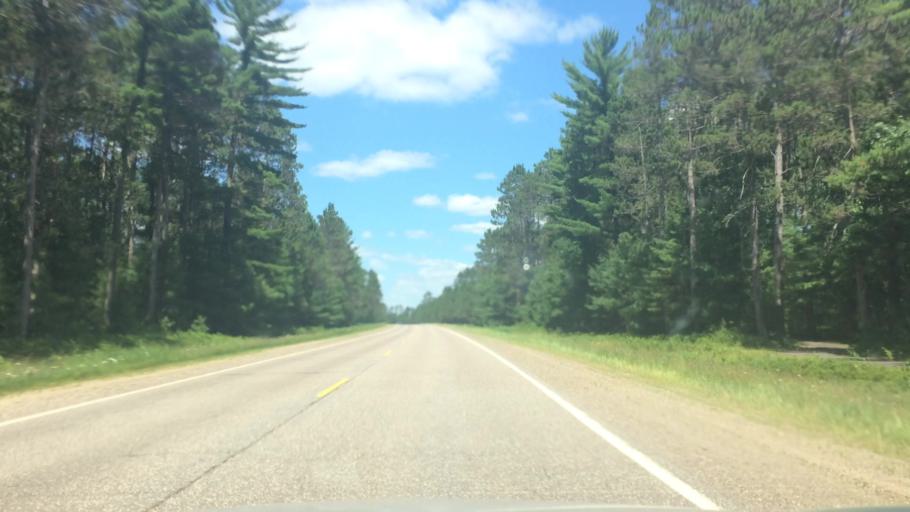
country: US
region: Wisconsin
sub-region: Vilas County
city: Lac du Flambeau
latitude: 46.0901
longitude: -89.6452
